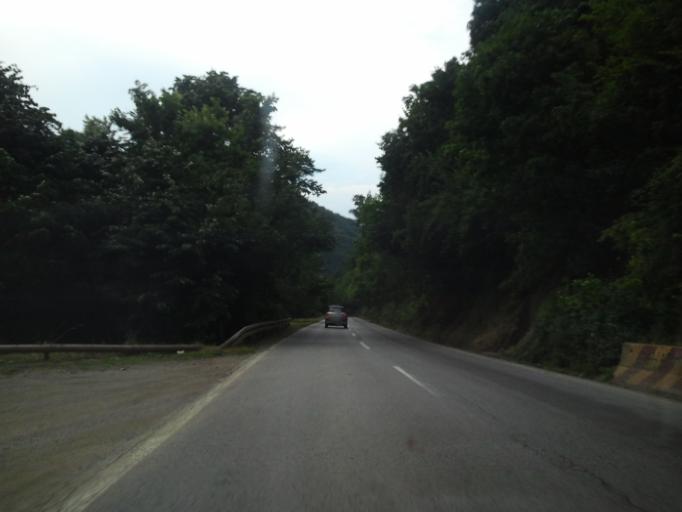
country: RS
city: Vrdnik
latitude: 45.1575
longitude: 19.8308
